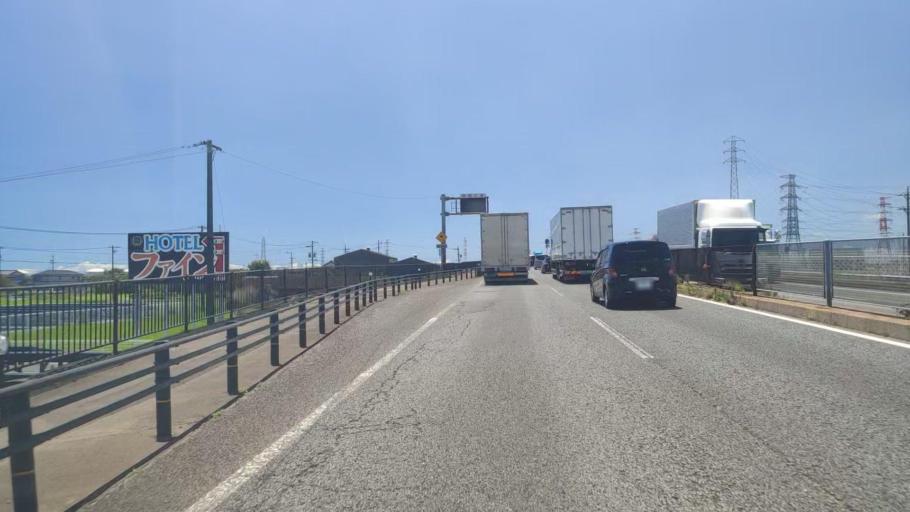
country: JP
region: Mie
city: Yokkaichi
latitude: 35.0368
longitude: 136.6898
